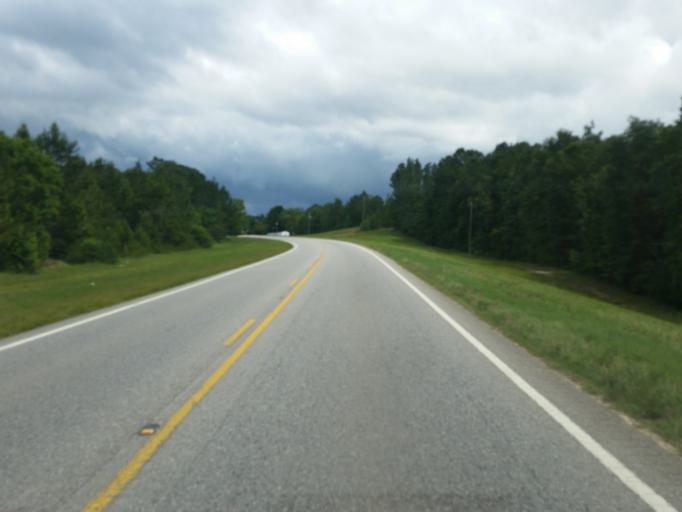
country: US
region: Mississippi
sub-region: George County
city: Lucedale
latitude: 30.8541
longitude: -88.4070
